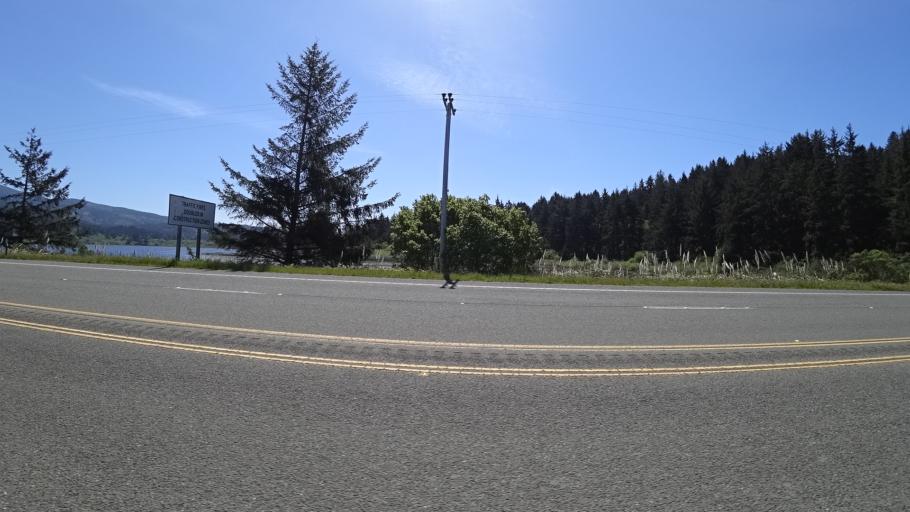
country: US
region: California
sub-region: Humboldt County
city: Westhaven-Moonstone
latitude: 41.1601
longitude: -124.1164
